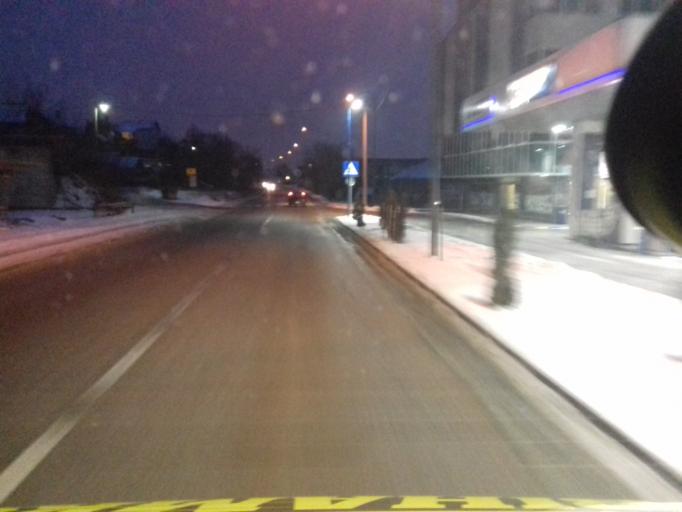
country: BA
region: Federation of Bosnia and Herzegovina
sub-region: Kanton Sarajevo
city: Sarajevo
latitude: 43.8606
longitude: 18.3189
